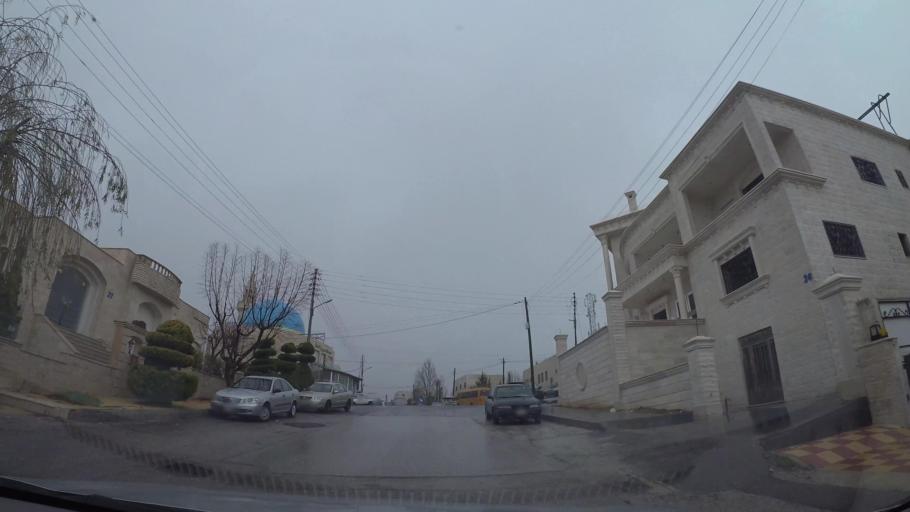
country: JO
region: Amman
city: Al Jubayhah
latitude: 32.0168
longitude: 35.8375
